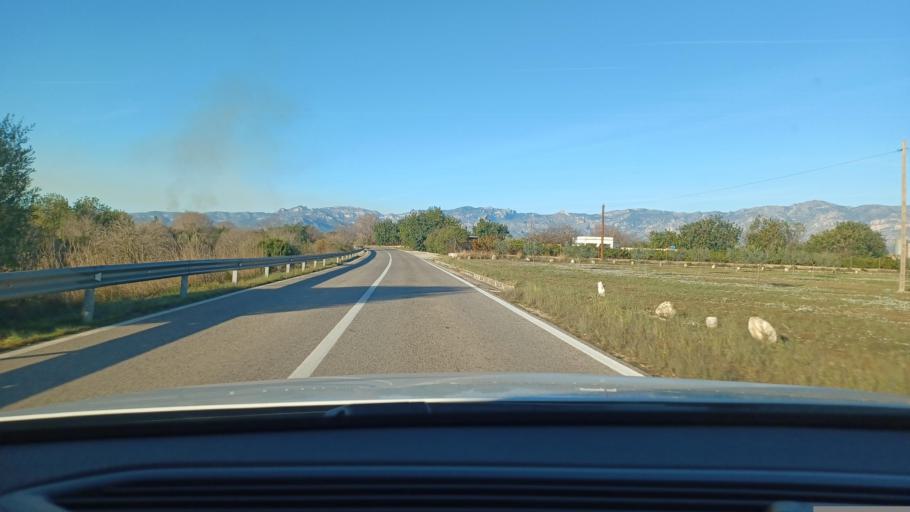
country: ES
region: Catalonia
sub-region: Provincia de Tarragona
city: Santa Barbara
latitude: 40.7155
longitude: 0.4807
